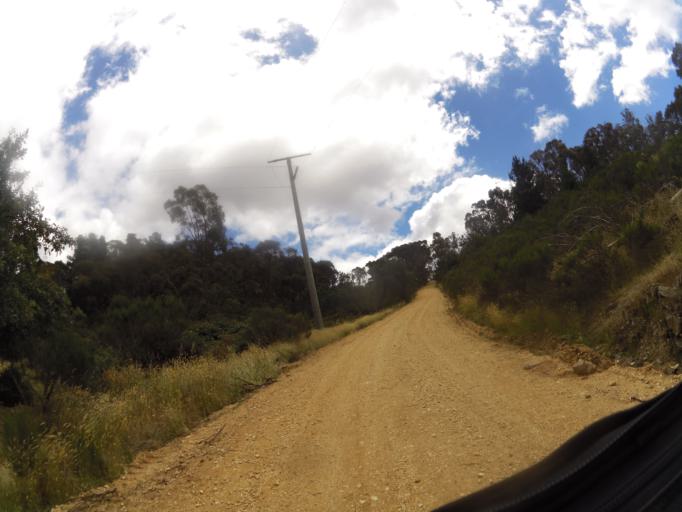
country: AU
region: Victoria
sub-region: Mount Alexander
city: Castlemaine
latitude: -37.0515
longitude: 144.2711
